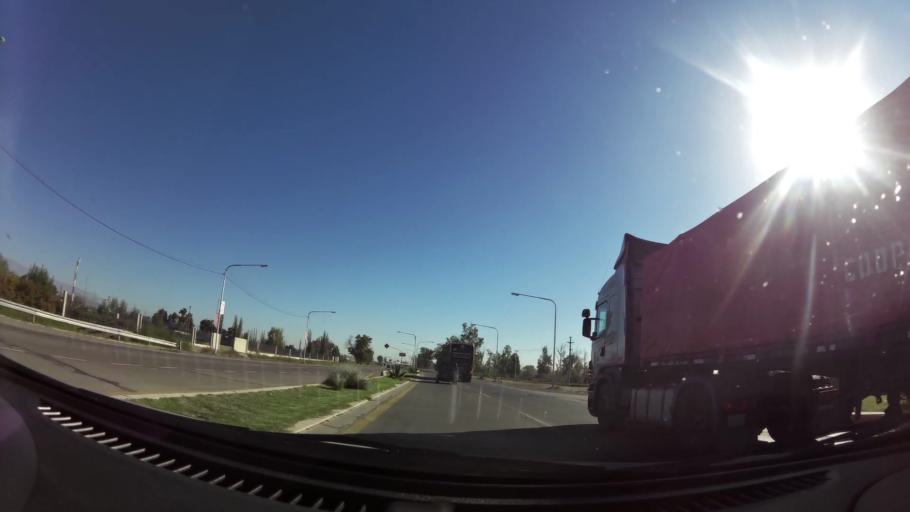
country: AR
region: Mendoza
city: Las Heras
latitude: -32.8272
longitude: -68.8043
